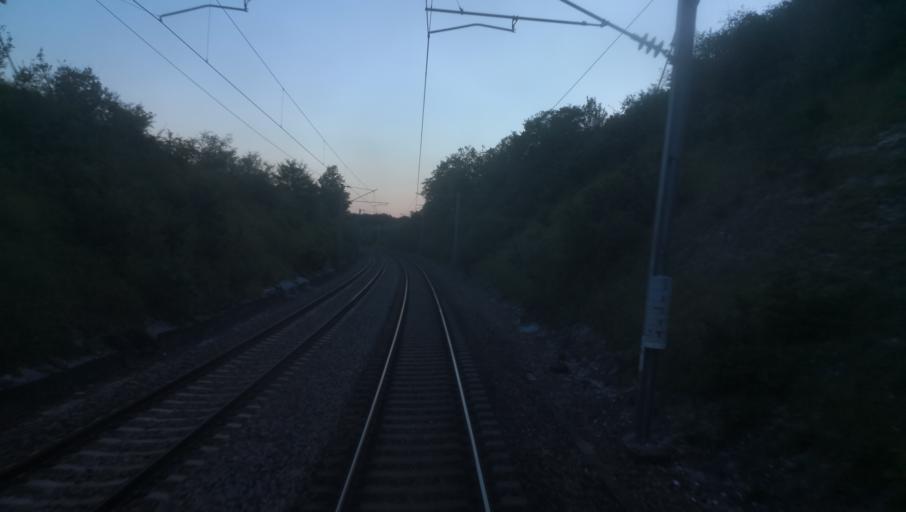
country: FR
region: Haute-Normandie
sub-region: Departement de l'Eure
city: Bueil
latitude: 48.9209
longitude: 1.4795
